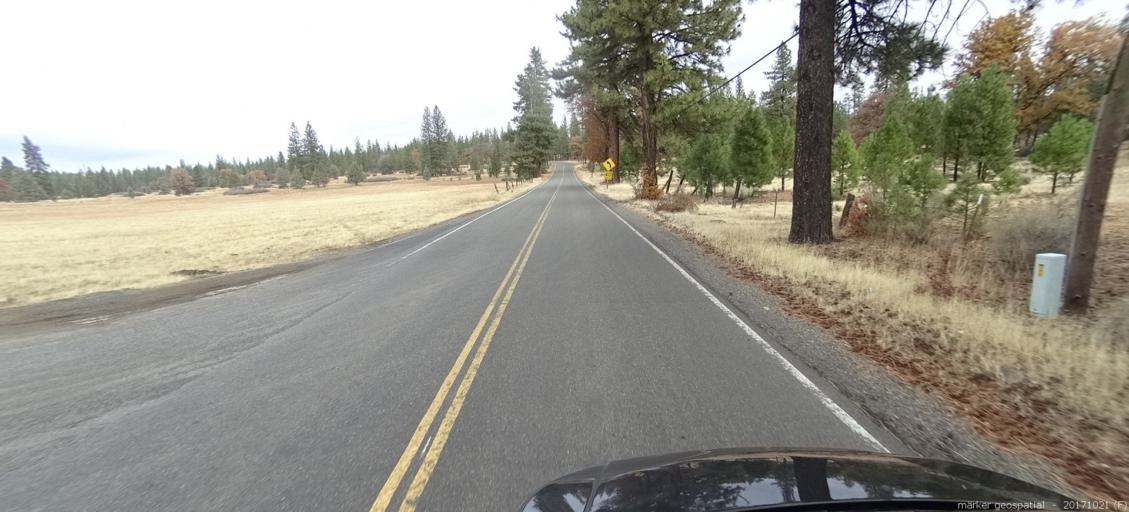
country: US
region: California
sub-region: Shasta County
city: Burney
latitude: 40.9406
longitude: -121.5690
